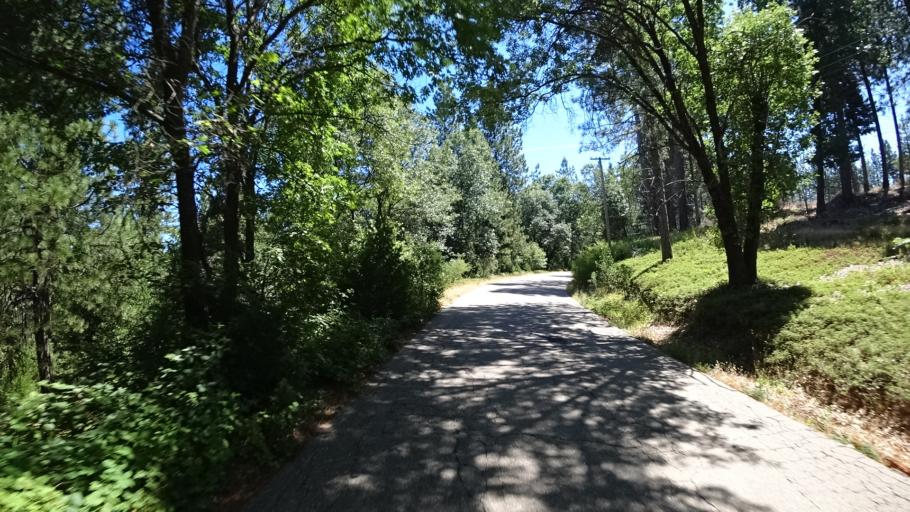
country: US
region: California
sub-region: Amador County
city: Pioneer
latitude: 38.4119
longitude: -120.5016
